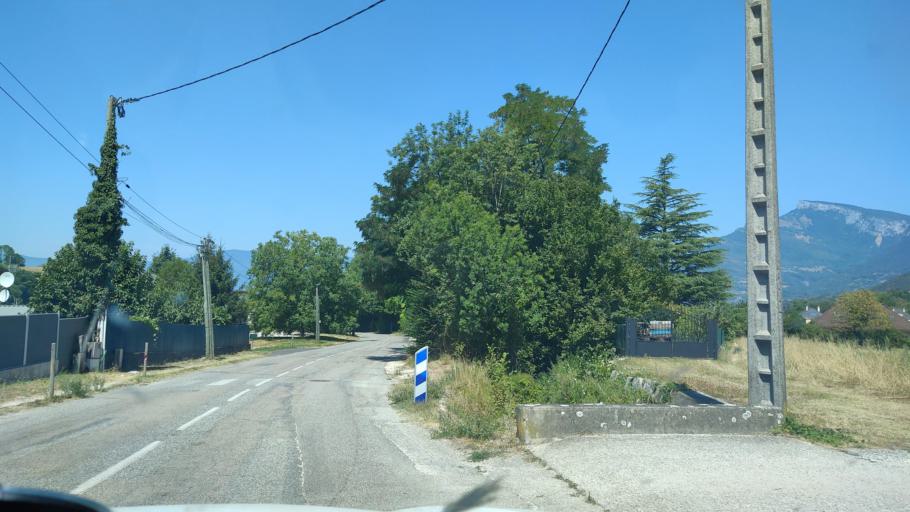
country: FR
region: Rhone-Alpes
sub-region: Departement de la Savoie
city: Challes-les-Eaux
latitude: 45.5386
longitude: 5.9931
